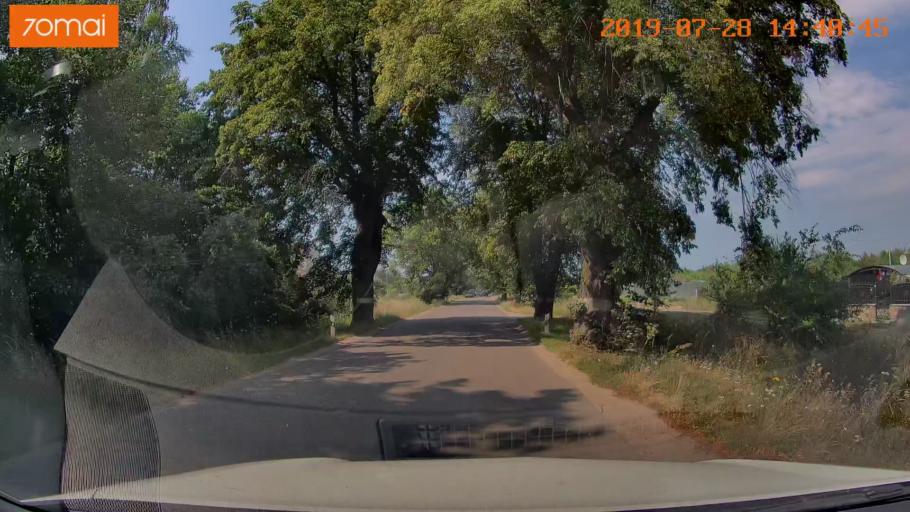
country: RU
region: Kaliningrad
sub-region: Gorod Kaliningrad
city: Yantarnyy
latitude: 54.8531
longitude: 19.9544
